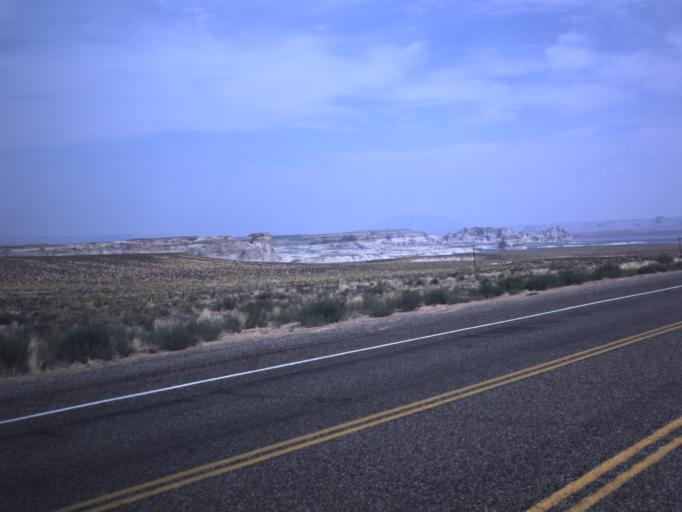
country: US
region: Arizona
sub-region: Coconino County
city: Page
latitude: 37.0332
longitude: -111.6098
